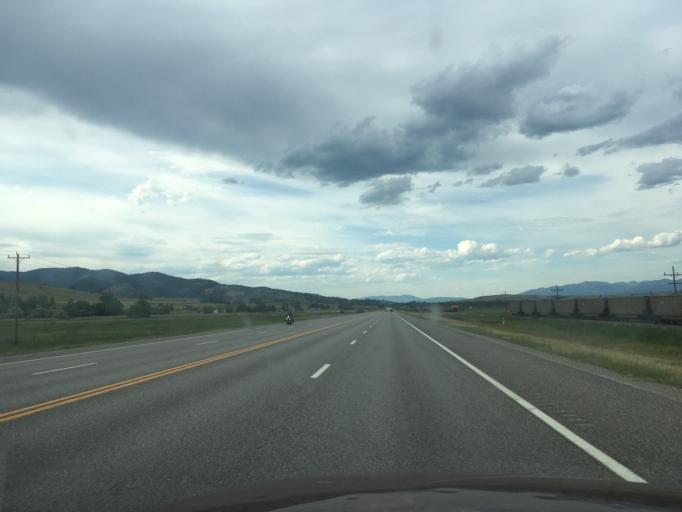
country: US
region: Montana
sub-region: Missoula County
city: Lolo
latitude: 46.7199
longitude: -114.0775
